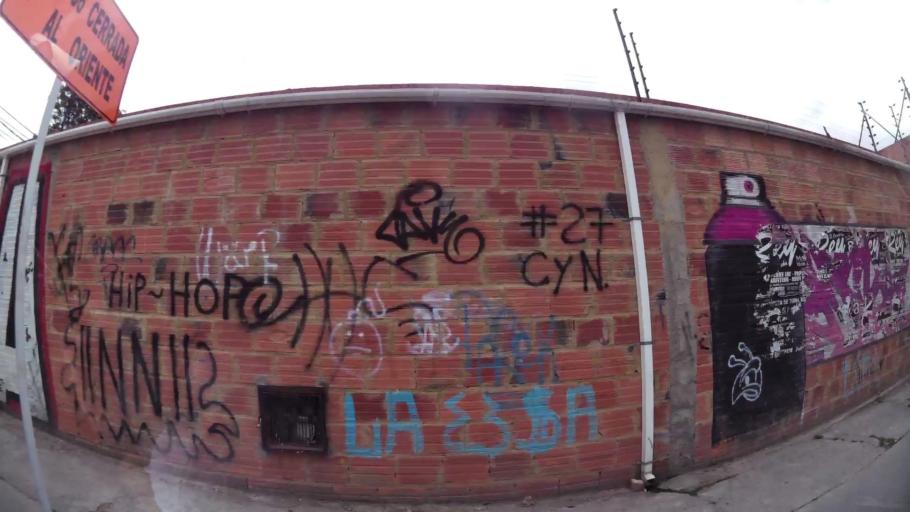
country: CO
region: Cundinamarca
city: La Calera
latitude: 4.7638
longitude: -74.0291
